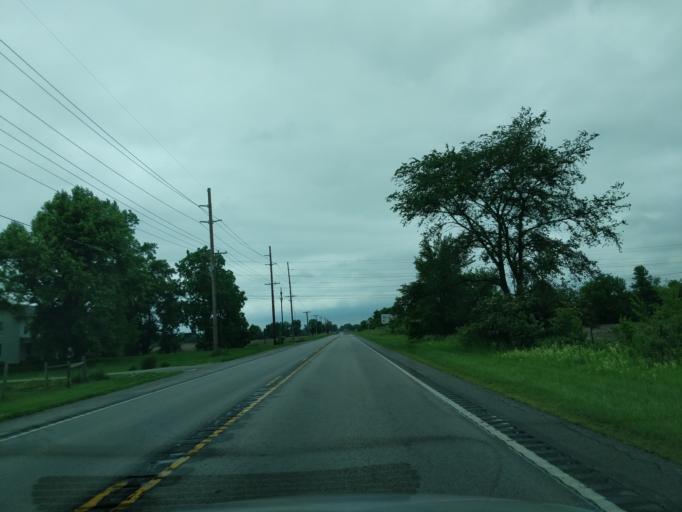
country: US
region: Indiana
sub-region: Hamilton County
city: Cicero
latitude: 40.1048
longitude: -86.0138
